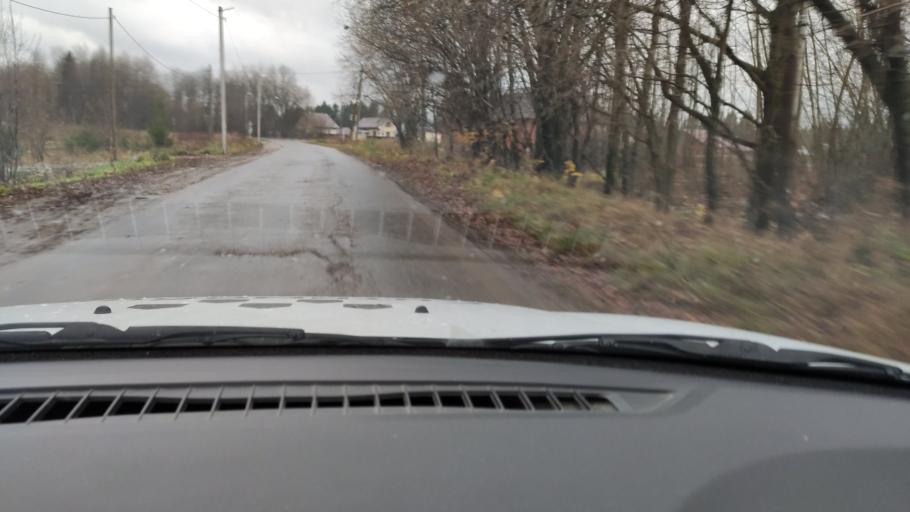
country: RU
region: Perm
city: Sylva
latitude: 58.0361
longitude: 56.7408
